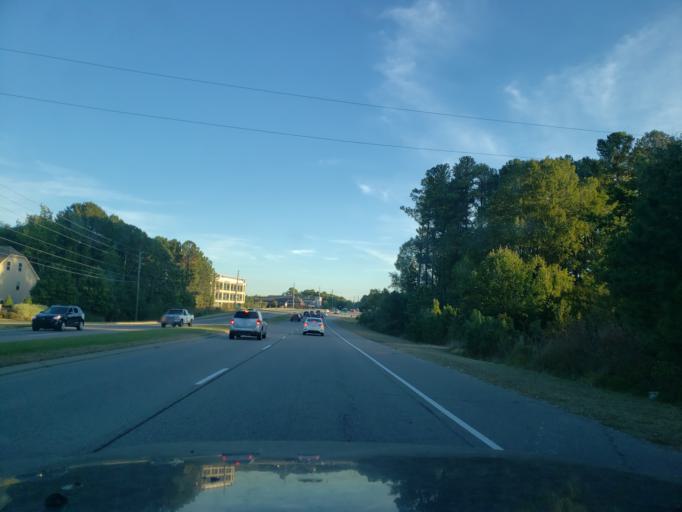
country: US
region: North Carolina
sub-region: Wake County
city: Morrisville
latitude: 35.8329
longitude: -78.8546
